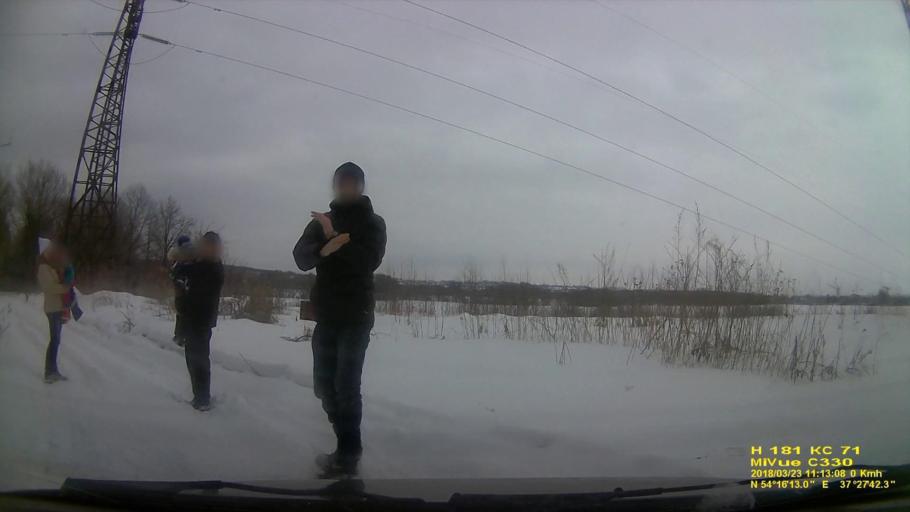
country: RU
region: Tula
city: Leninskiy
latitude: 54.2691
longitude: 37.4622
